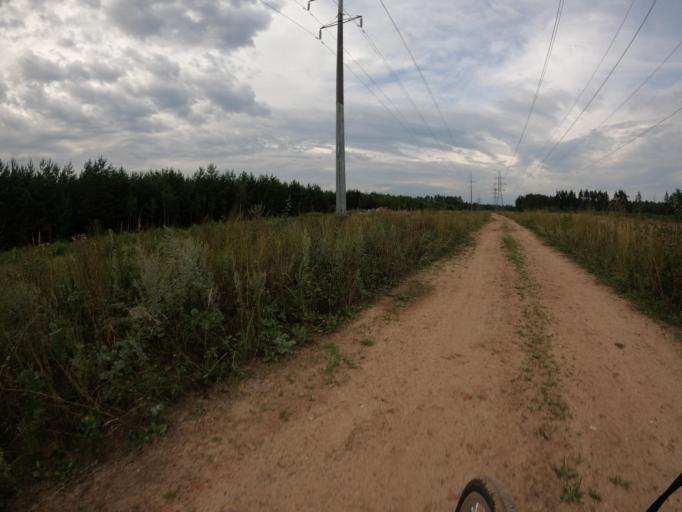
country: RU
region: Moskovskaya
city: Rodniki
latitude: 55.6758
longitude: 38.0847
